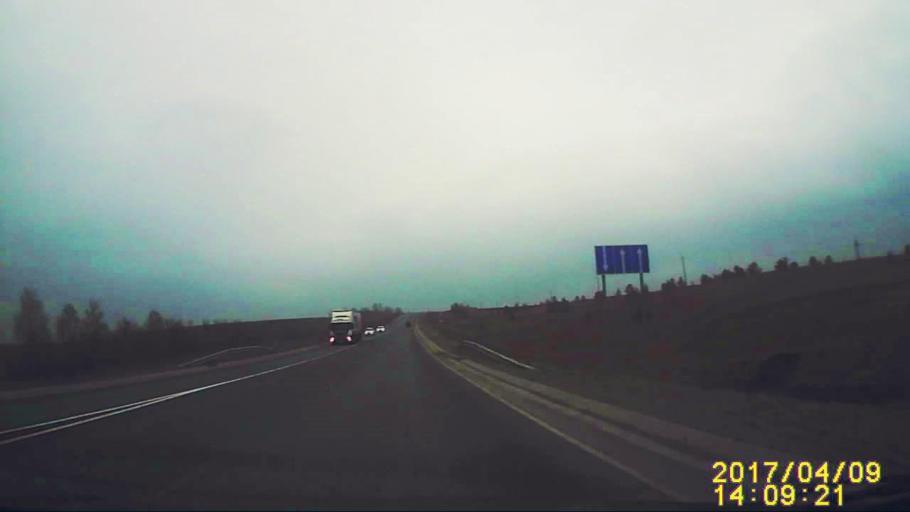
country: RU
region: Ulyanovsk
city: Krasnyy Gulyay
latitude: 54.0276
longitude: 48.2132
